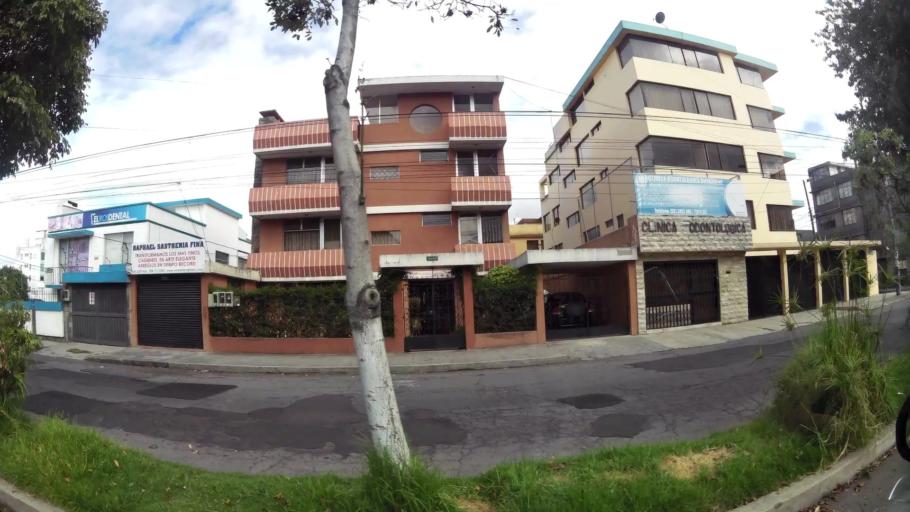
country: EC
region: Pichincha
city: Quito
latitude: -0.1642
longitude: -78.4765
